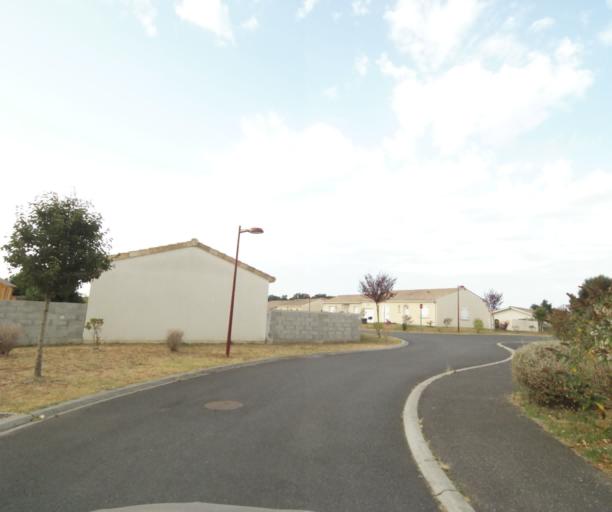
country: FR
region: Aquitaine
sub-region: Departement de la Gironde
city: Creon
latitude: 44.7692
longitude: -0.3571
